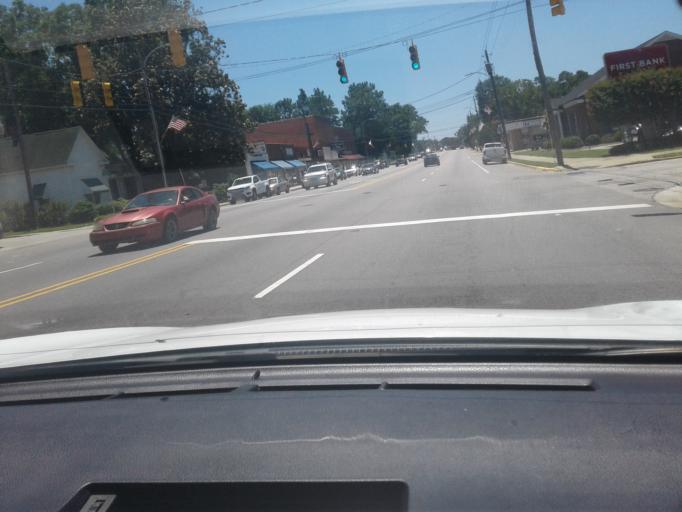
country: US
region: North Carolina
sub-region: Harnett County
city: Lillington
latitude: 35.3969
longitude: -78.8170
